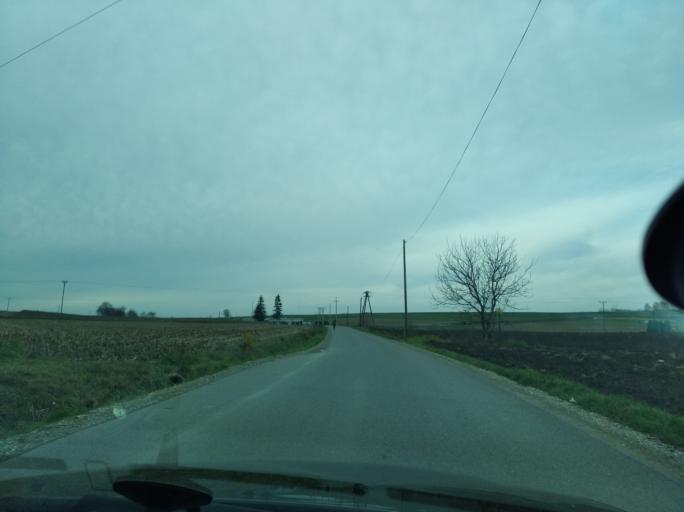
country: PL
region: Subcarpathian Voivodeship
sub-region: Powiat przeworski
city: Przeworsk
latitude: 50.0637
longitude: 22.4724
